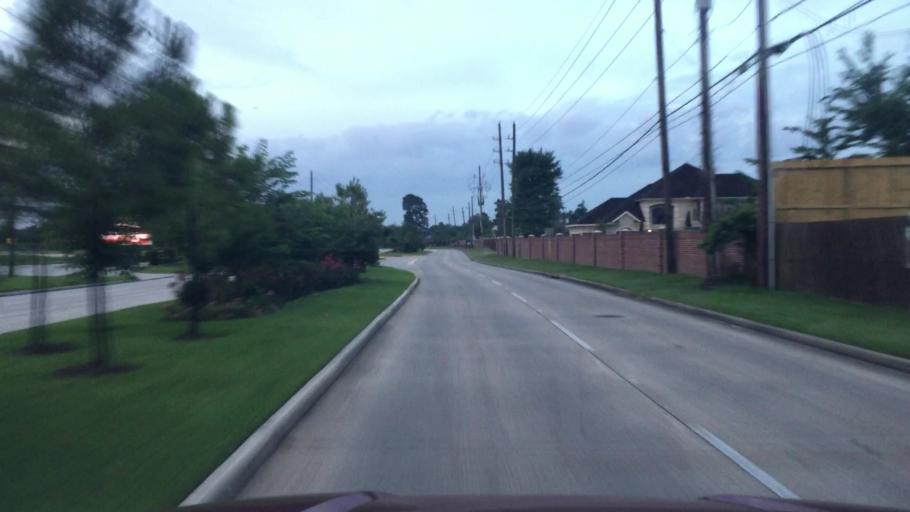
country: US
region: Texas
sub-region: Harris County
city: Tomball
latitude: 30.0370
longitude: -95.5364
